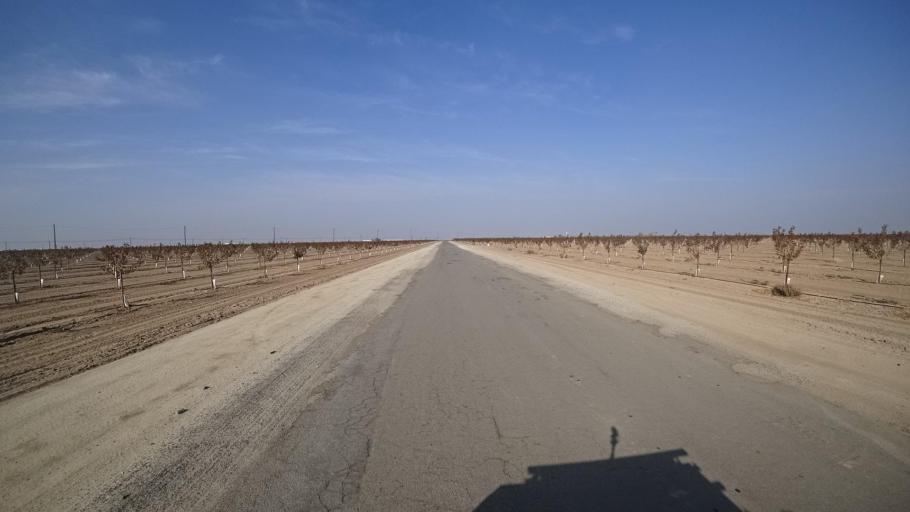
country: US
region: California
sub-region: Tulare County
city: Richgrove
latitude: 35.7829
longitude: -119.1170
